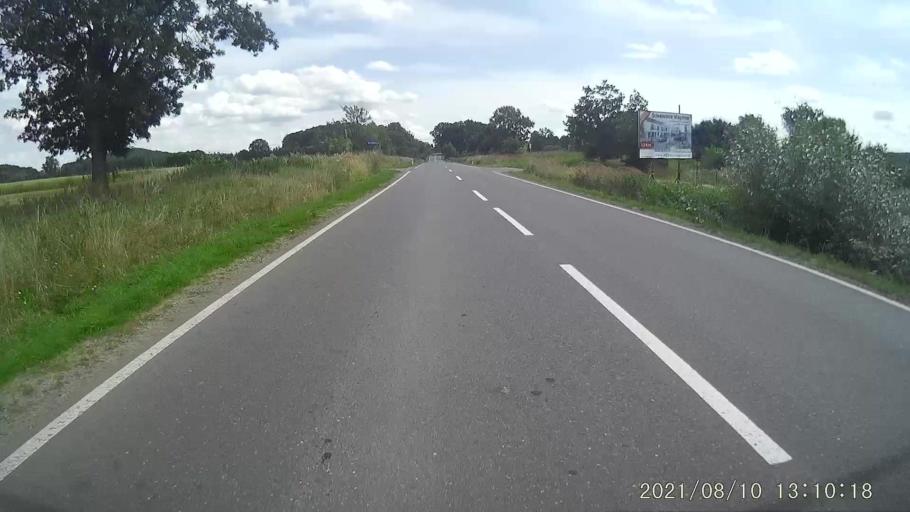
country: PL
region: Lower Silesian Voivodeship
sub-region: Powiat klodzki
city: Bozkow
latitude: 50.5023
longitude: 16.5313
